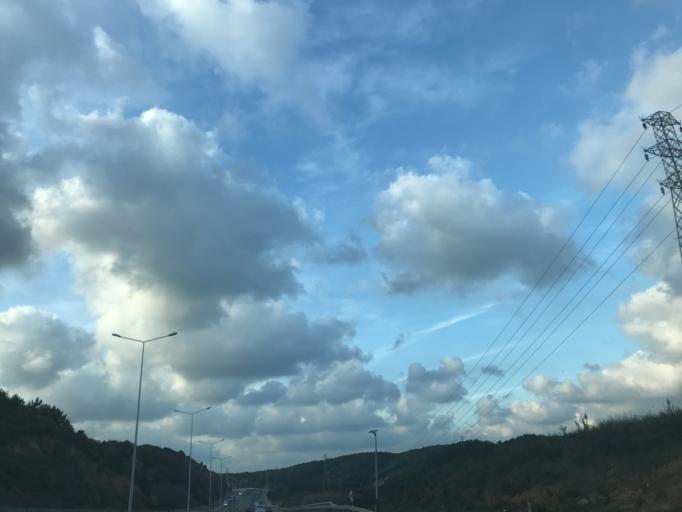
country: TR
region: Istanbul
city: Kemerburgaz
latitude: 41.1887
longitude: 28.8697
